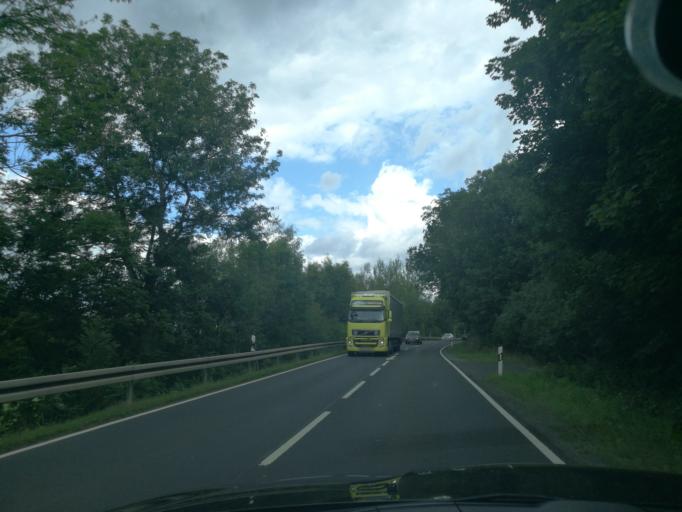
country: DE
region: Saxony
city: Oelsnitz
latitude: 50.3969
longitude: 12.1878
